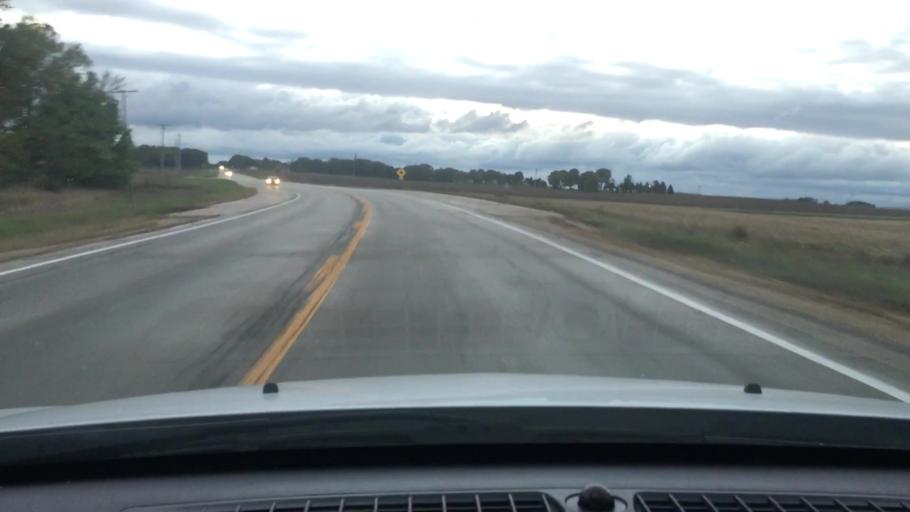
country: US
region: Illinois
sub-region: DeKalb County
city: Malta
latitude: 41.9361
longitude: -88.8087
